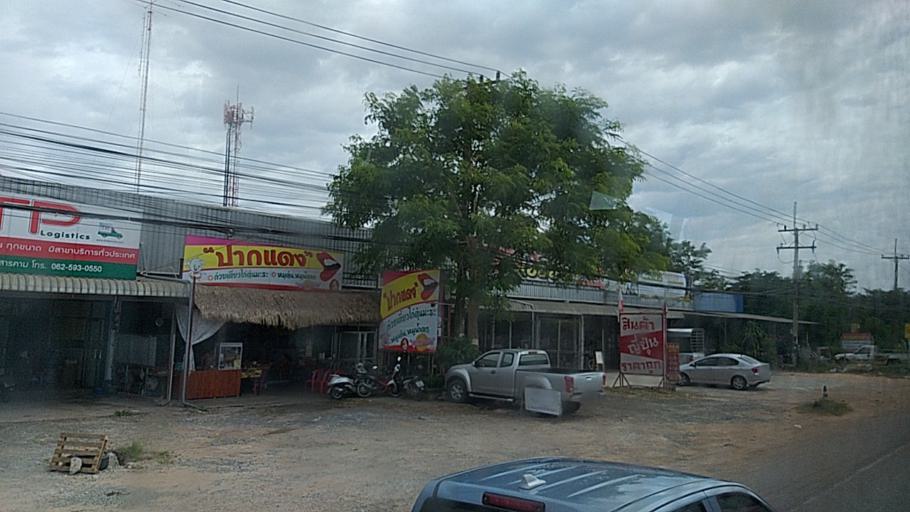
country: TH
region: Maha Sarakham
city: Maha Sarakham
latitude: 16.2069
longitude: 103.2861
